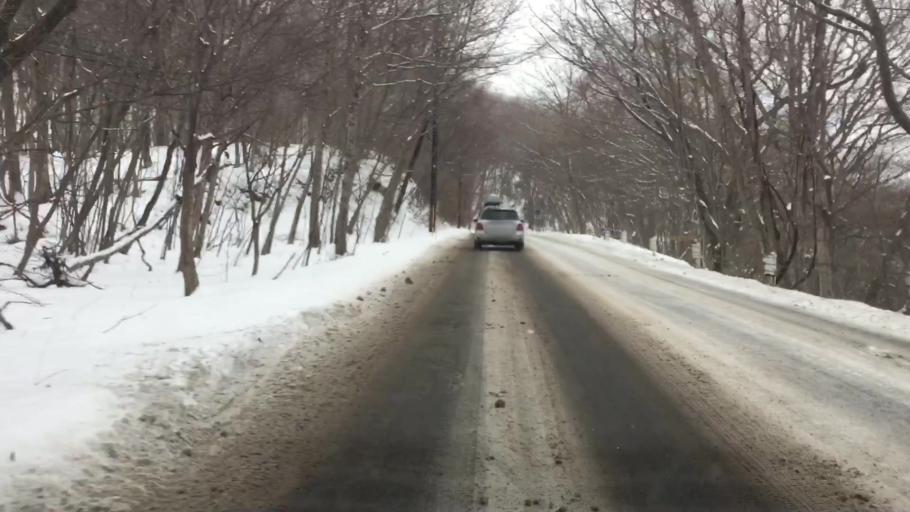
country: JP
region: Tochigi
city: Yaita
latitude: 36.9679
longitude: 139.7884
